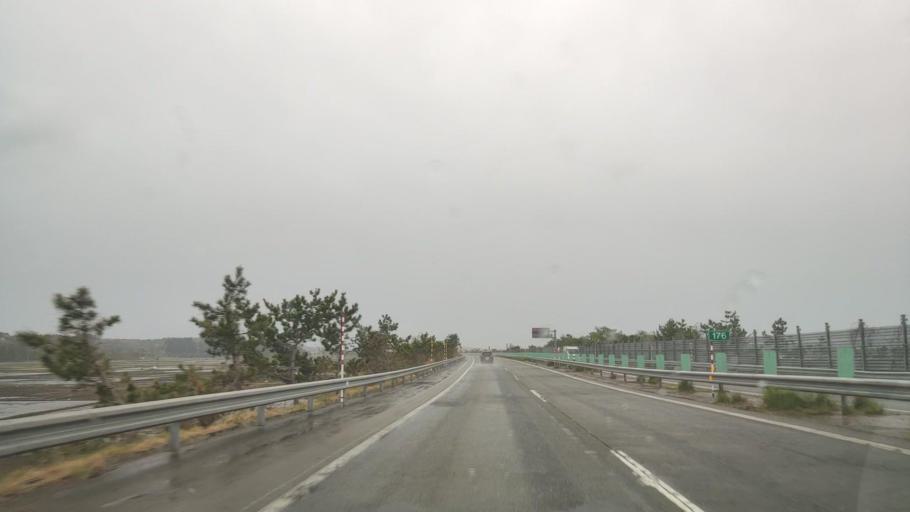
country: JP
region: Akita
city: Noshiromachi
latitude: 40.1838
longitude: 140.0775
